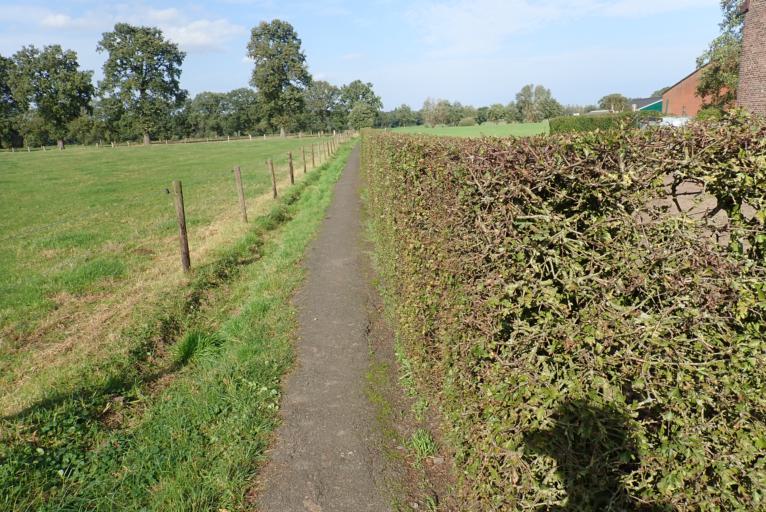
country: BE
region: Flanders
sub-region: Provincie Antwerpen
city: Essen
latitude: 51.4293
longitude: 4.4687
